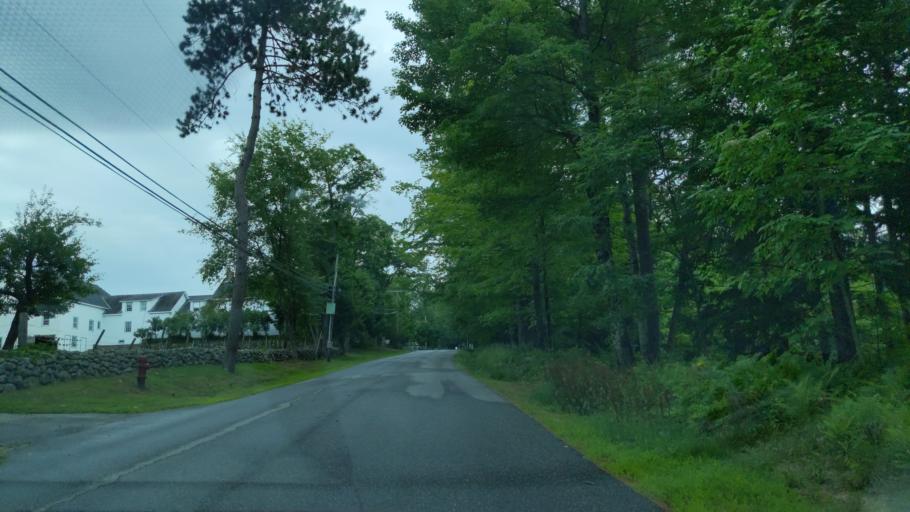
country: US
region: New Hampshire
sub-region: Merrimack County
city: New London
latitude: 43.4222
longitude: -72.0283
